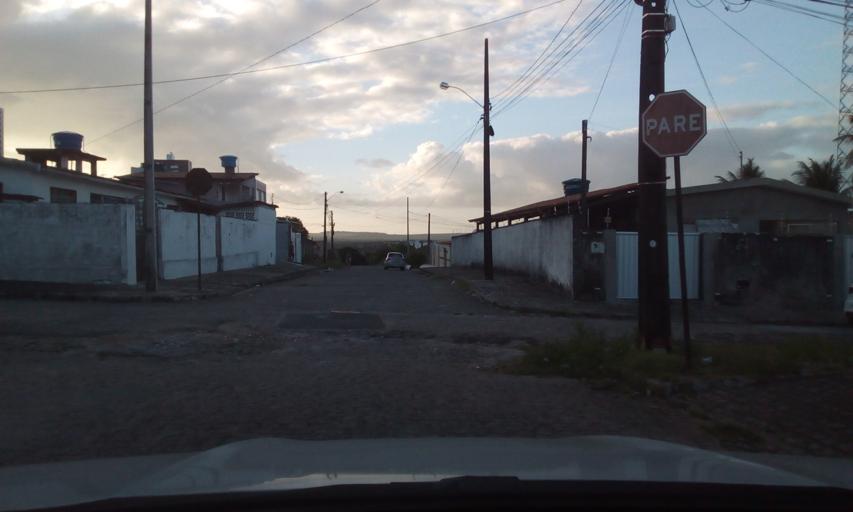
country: BR
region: Paraiba
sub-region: Joao Pessoa
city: Joao Pessoa
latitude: -7.1102
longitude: -34.8621
